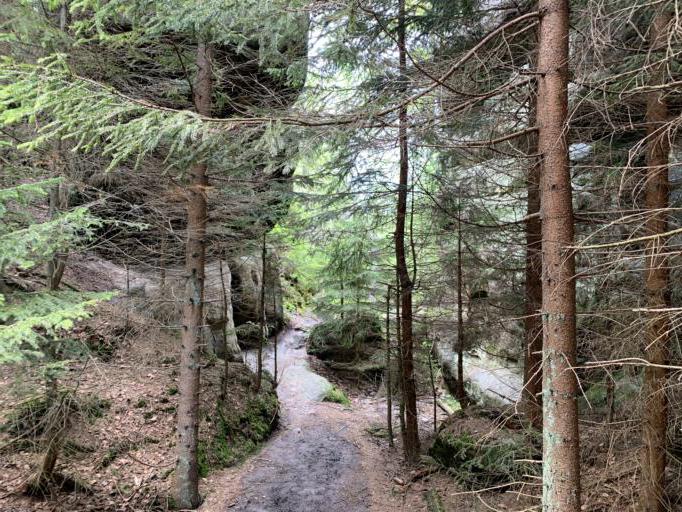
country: PL
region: Lower Silesian Voivodeship
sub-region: Powiat klodzki
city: Radkow
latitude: 50.4576
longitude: 16.3636
